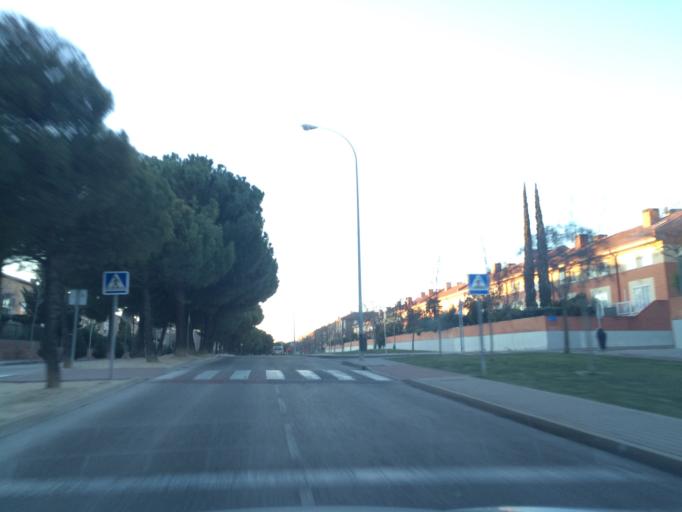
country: ES
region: Madrid
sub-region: Provincia de Madrid
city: Tres Cantos
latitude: 40.5982
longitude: -3.7074
